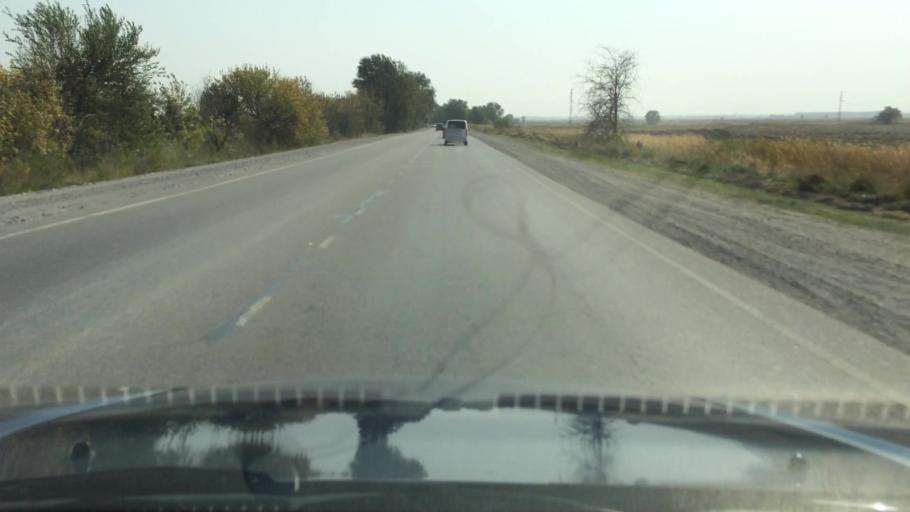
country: KG
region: Chuy
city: Lebedinovka
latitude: 42.9246
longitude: 74.7023
